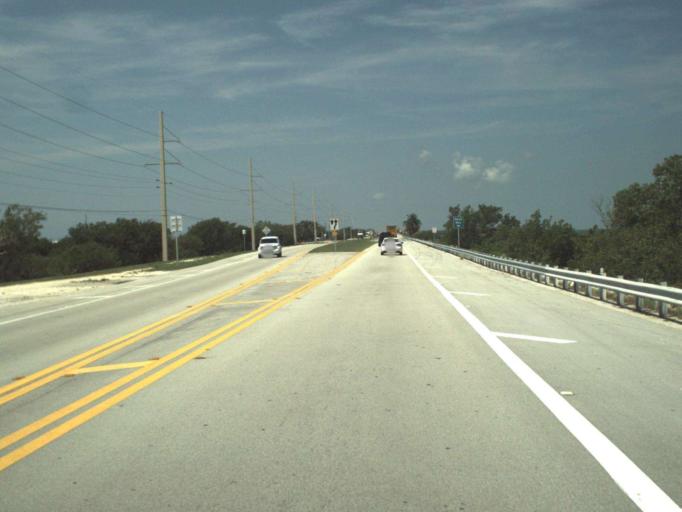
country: US
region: Florida
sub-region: Monroe County
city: Marathon
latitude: 24.7815
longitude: -80.9116
